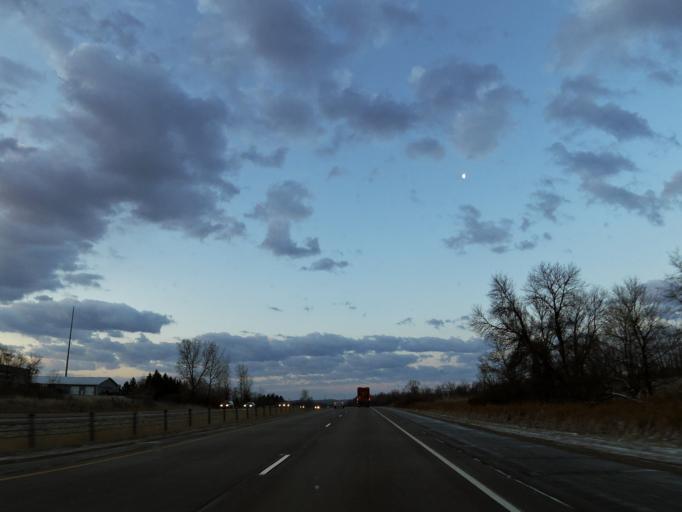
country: US
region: Minnesota
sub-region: Dakota County
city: Lakeville
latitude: 44.6229
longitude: -93.2984
